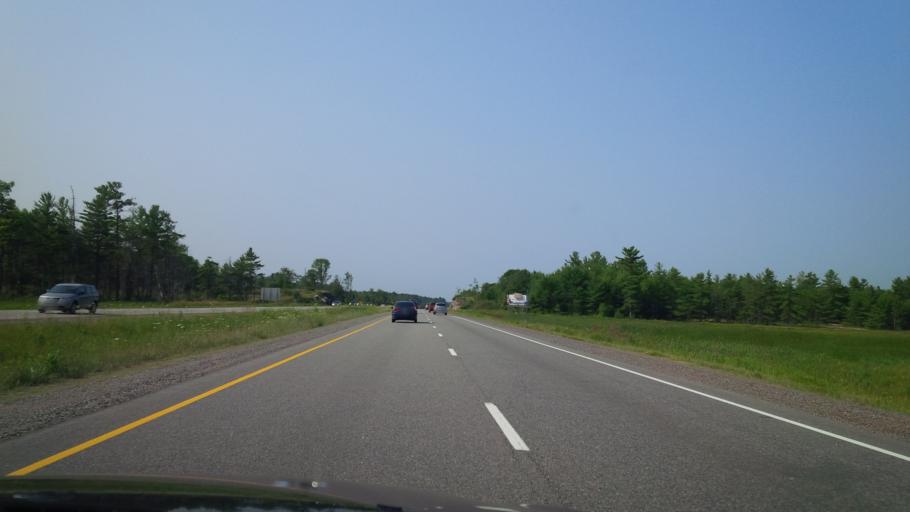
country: CA
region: Ontario
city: Gravenhurst
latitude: 44.9644
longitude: -79.3241
